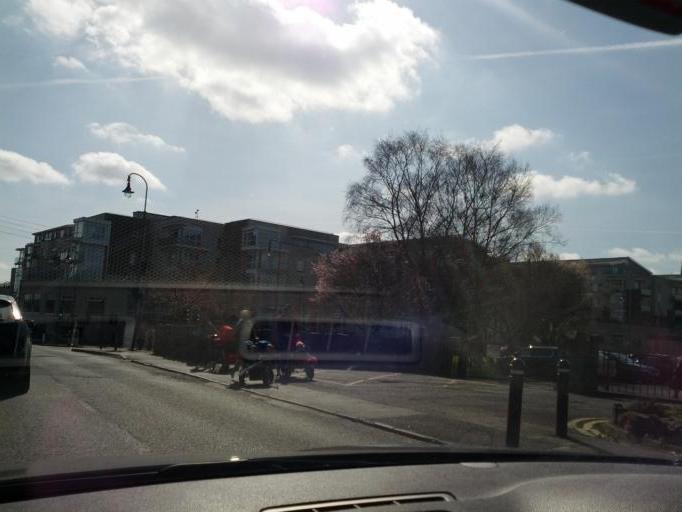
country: IE
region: Leinster
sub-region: Kildare
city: Maynooth
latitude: 53.3835
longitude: -6.5944
